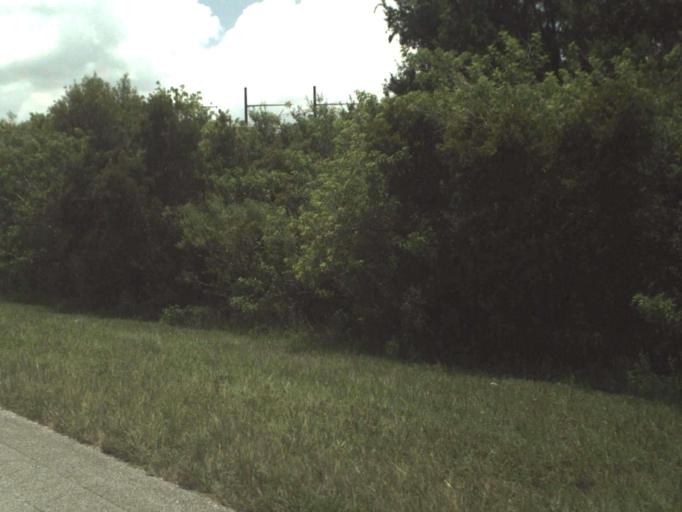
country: US
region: Florida
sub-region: Saint Lucie County
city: Fort Pierce South
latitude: 27.3744
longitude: -80.4198
